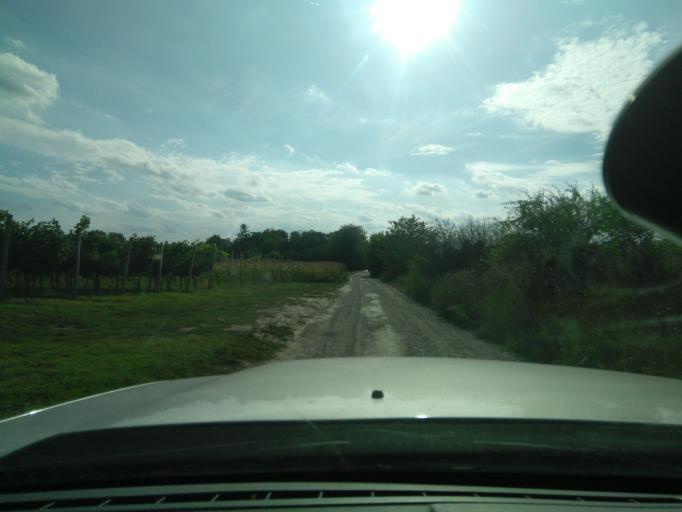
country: HU
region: Fejer
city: Bicske
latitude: 47.4971
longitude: 18.6534
